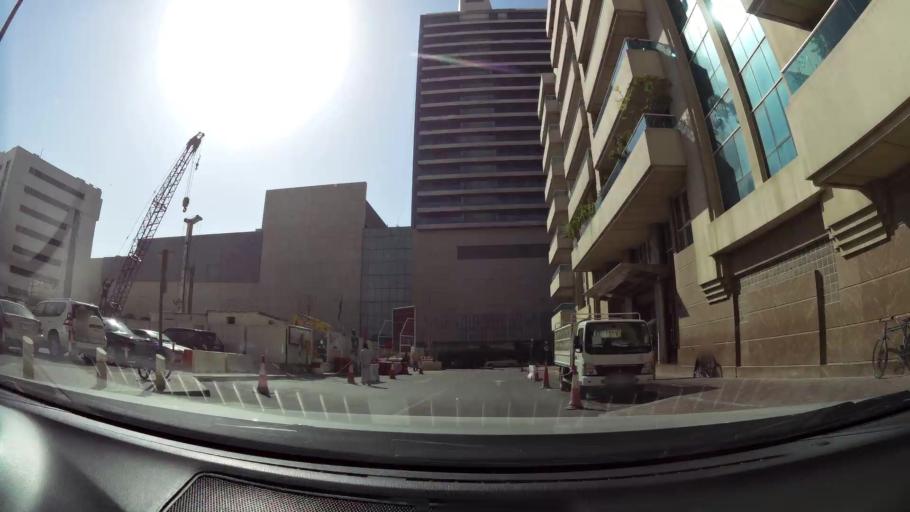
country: AE
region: Ash Shariqah
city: Sharjah
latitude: 25.2536
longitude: 55.3011
